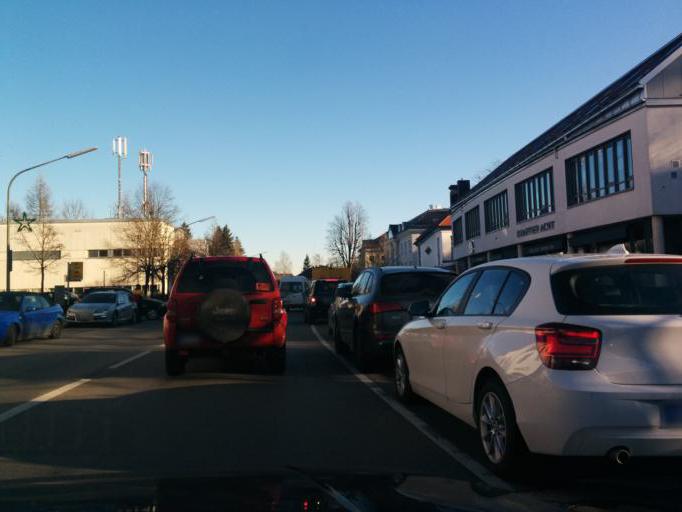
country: DE
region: Bavaria
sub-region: Upper Bavaria
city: Grunwald
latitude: 48.0410
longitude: 11.5252
